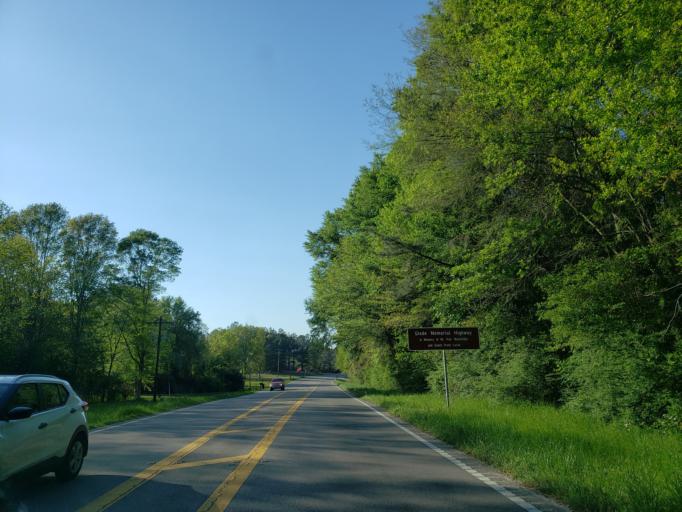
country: US
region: Mississippi
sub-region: Jones County
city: Laurel
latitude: 31.6515
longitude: -89.1045
